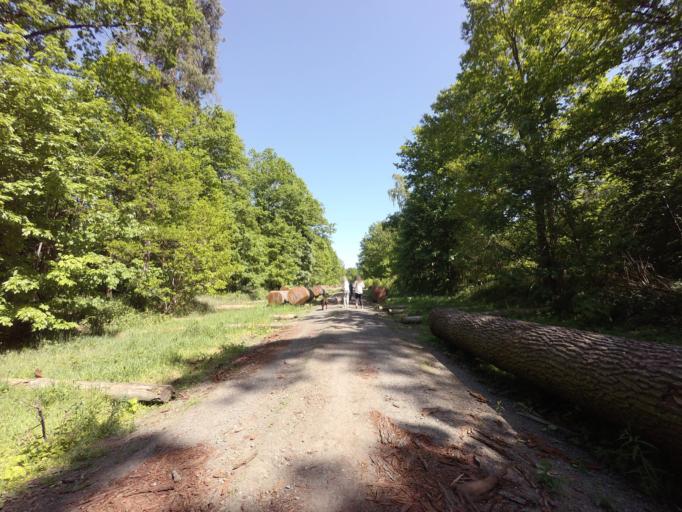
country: DE
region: Lower Saxony
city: Lehre
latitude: 52.3163
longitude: 10.6425
